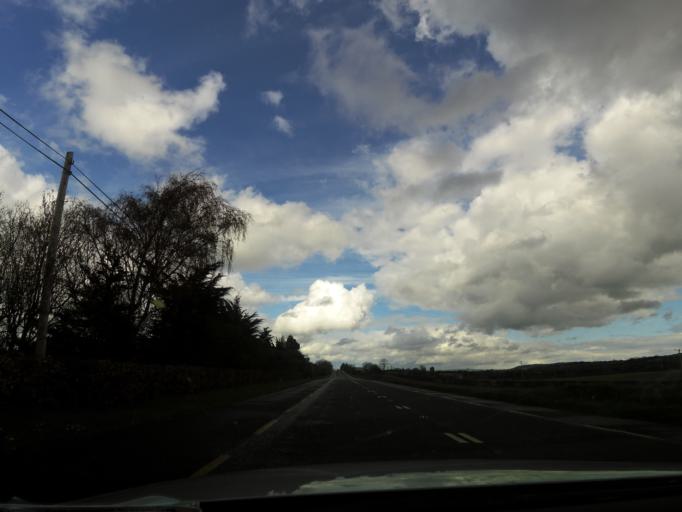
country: IE
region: Leinster
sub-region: Laois
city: Rathdowney
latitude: 52.8111
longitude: -7.4874
